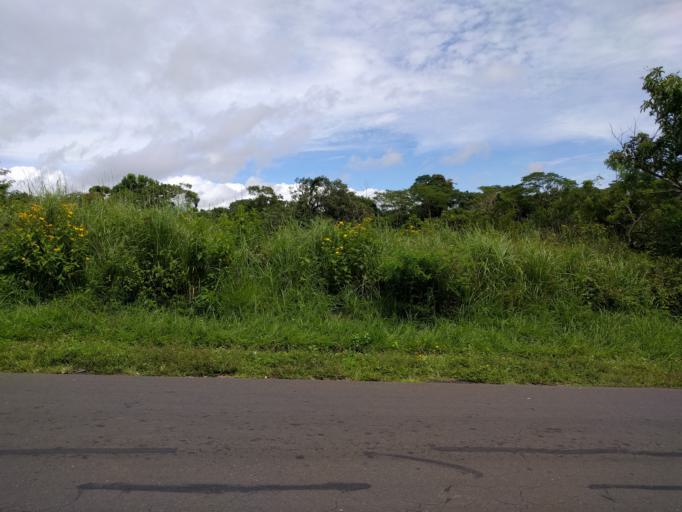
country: GT
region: Escuintla
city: San Vicente Pacaya
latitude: 14.3214
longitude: -90.5586
